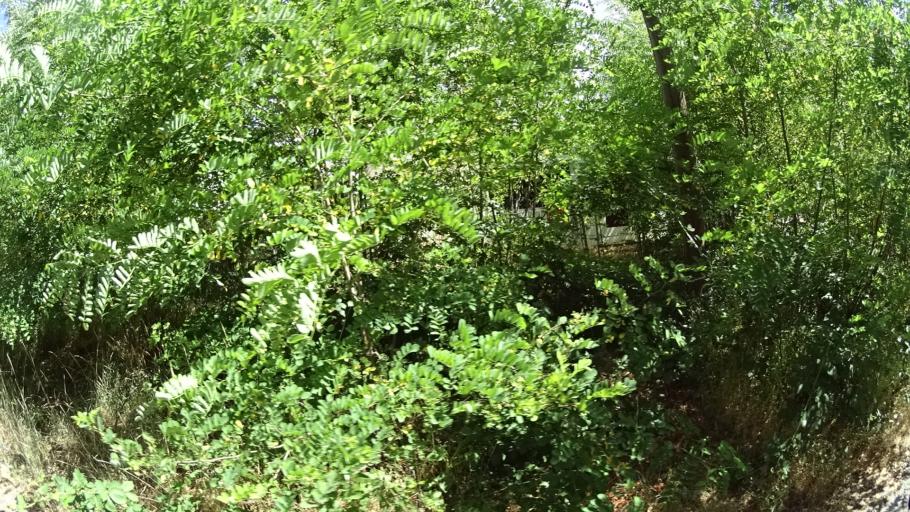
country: US
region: California
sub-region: Amador County
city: Pioneer
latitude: 38.3368
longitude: -120.5162
